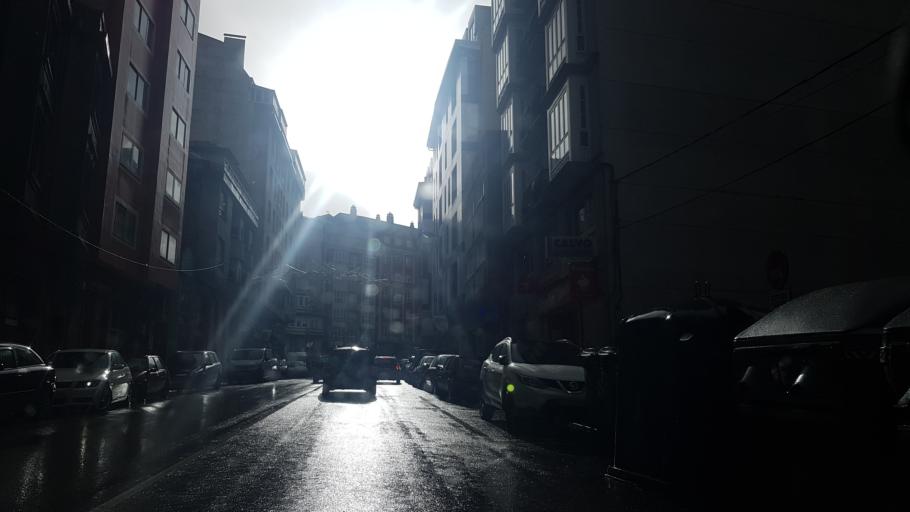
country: ES
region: Galicia
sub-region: Provincia de Lugo
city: Vilalba
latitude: 43.3003
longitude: -7.6787
